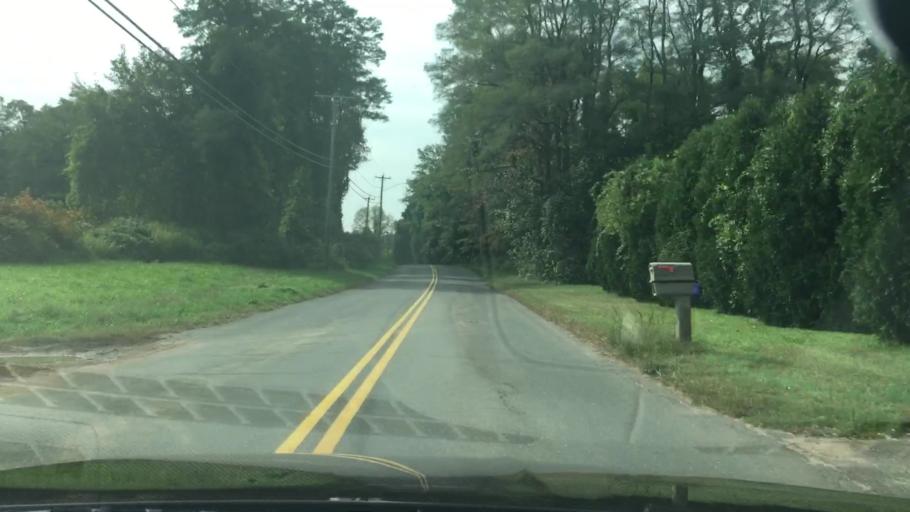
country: US
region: Connecticut
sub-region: Hartford County
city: Broad Brook
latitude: 41.8886
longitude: -72.5388
